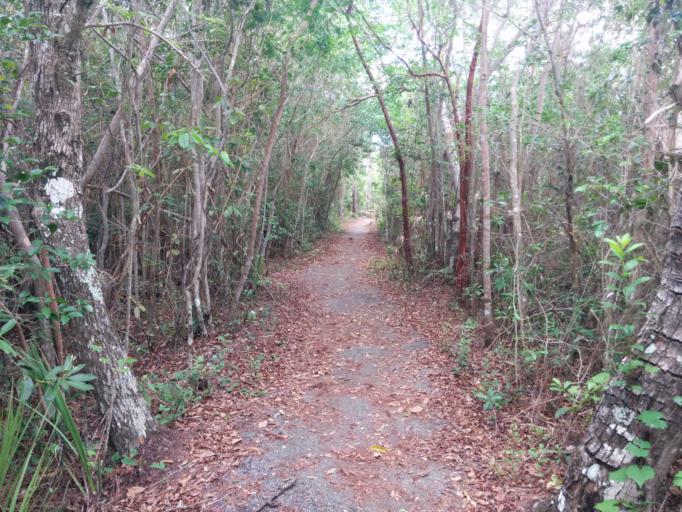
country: US
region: Florida
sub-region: Miami-Dade County
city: Florida City
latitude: 25.4246
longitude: -80.6796
